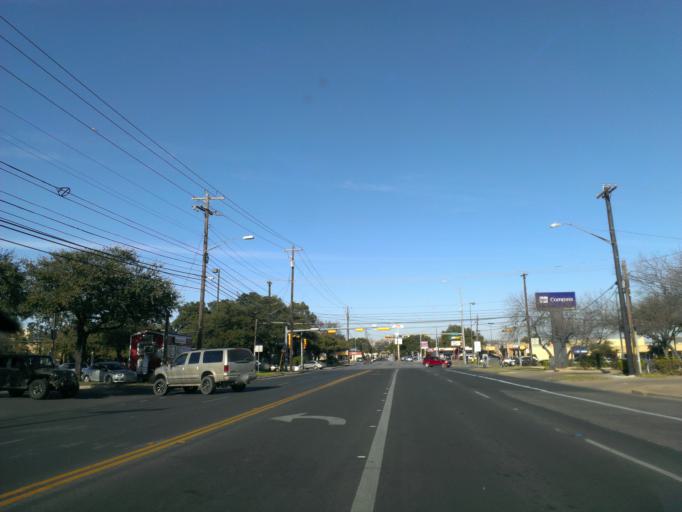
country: US
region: Texas
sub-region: Travis County
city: Austin
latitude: 30.2381
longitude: -97.7541
